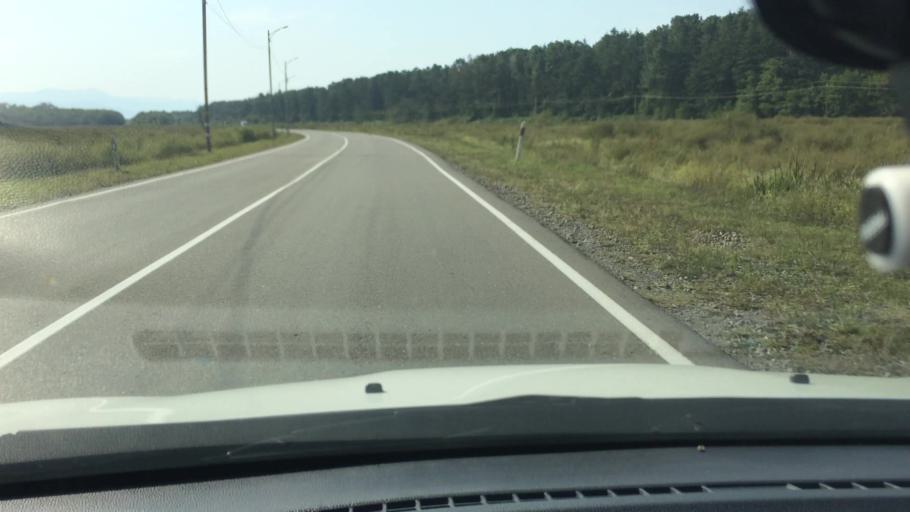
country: GE
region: Guria
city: Urek'i
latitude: 41.9537
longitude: 41.7708
